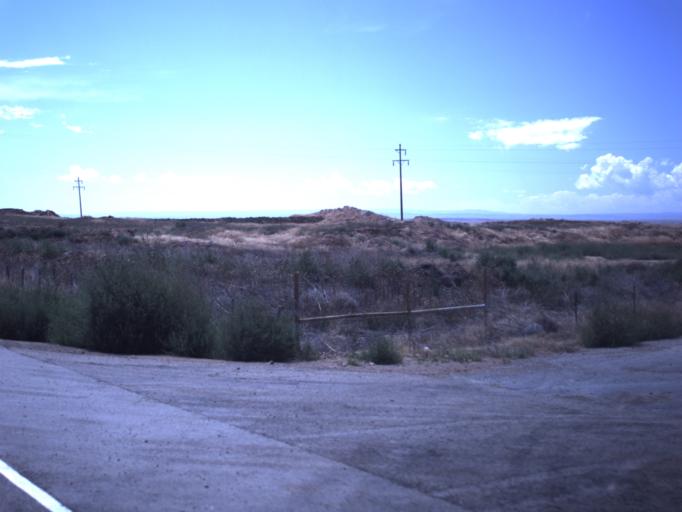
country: US
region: Utah
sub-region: Uintah County
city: Maeser
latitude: 40.2288
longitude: -109.6844
